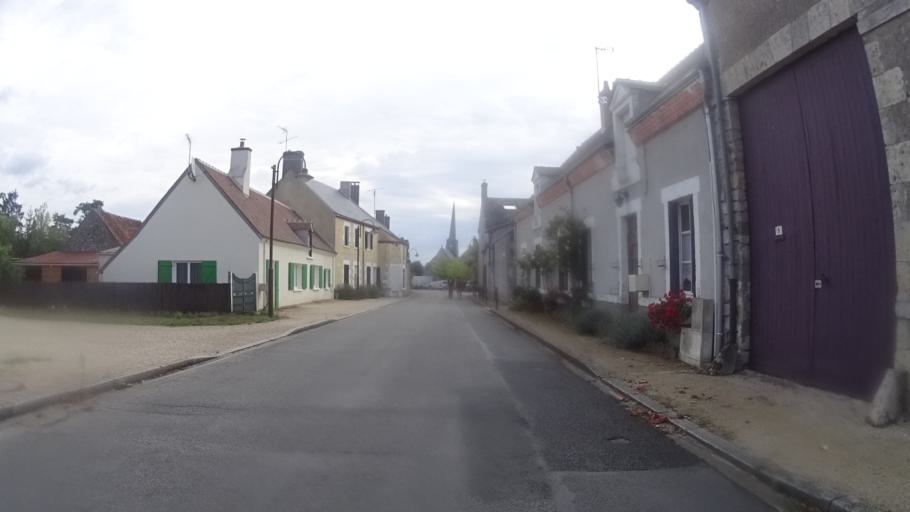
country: FR
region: Centre
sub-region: Departement du Loiret
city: Vitry-aux-Loges
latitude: 47.9910
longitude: 2.2122
